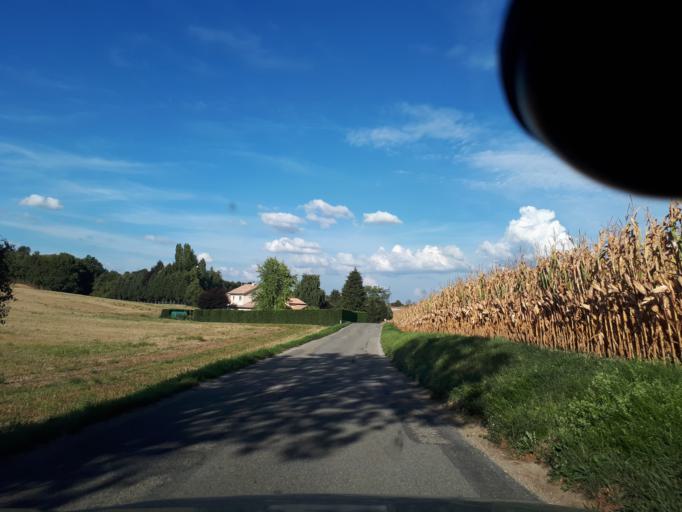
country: FR
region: Rhone-Alpes
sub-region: Departement de l'Isere
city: Chatonnay
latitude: 45.5105
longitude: 5.2267
